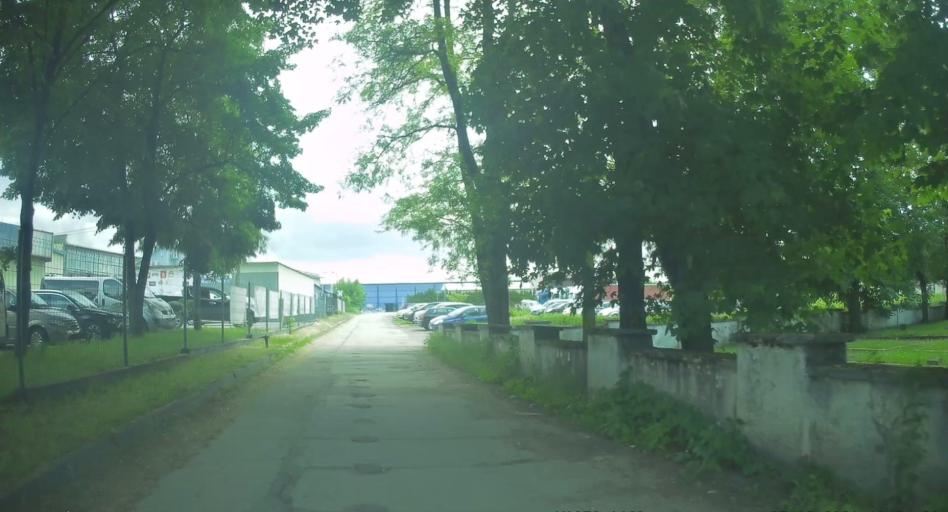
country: PL
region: Subcarpathian Voivodeship
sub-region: Powiat debicki
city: Debica
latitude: 50.0590
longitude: 21.4342
